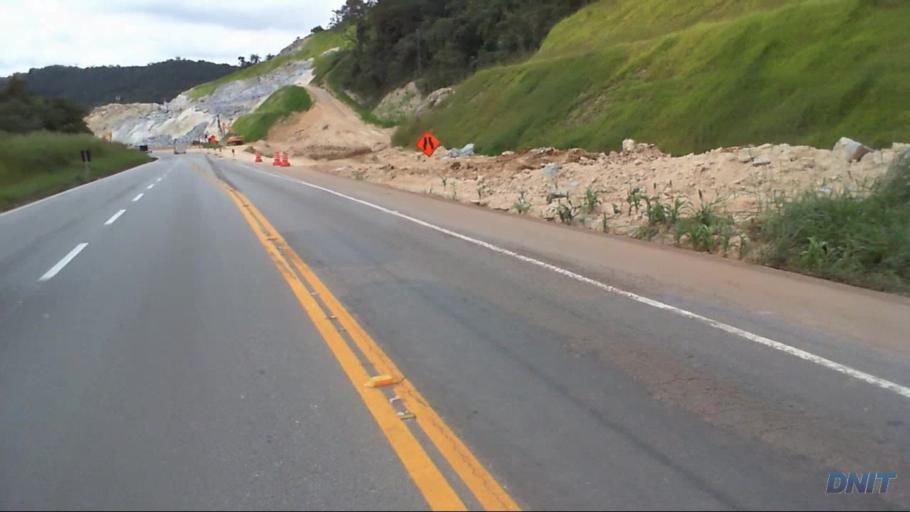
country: BR
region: Minas Gerais
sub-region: Caete
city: Caete
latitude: -19.7868
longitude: -43.6701
